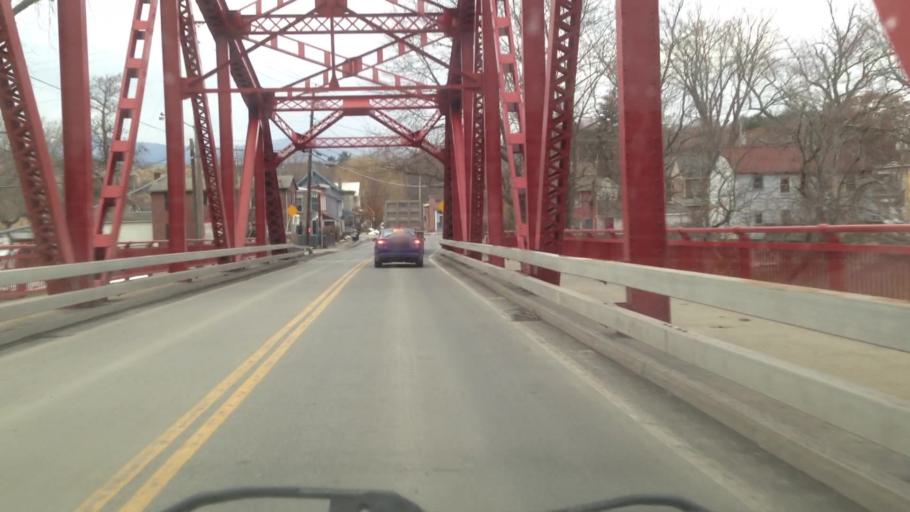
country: US
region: New York
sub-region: Ulster County
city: Saugerties
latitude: 42.0714
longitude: -73.9502
